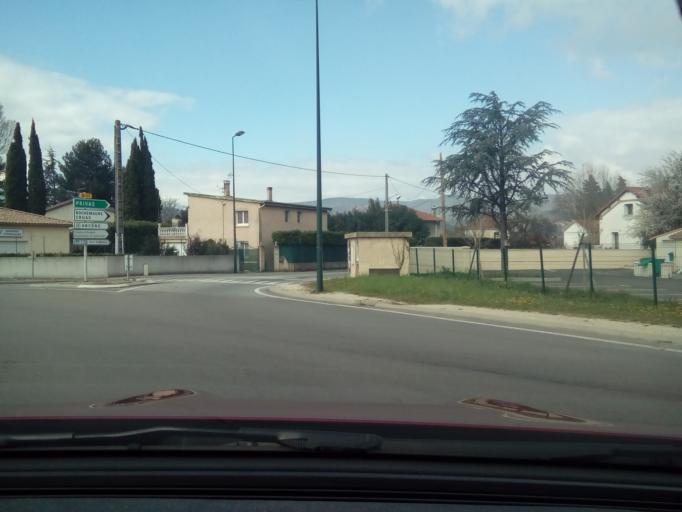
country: FR
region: Rhone-Alpes
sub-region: Departement de la Drome
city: Montelimar
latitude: 44.5664
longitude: 4.7356
